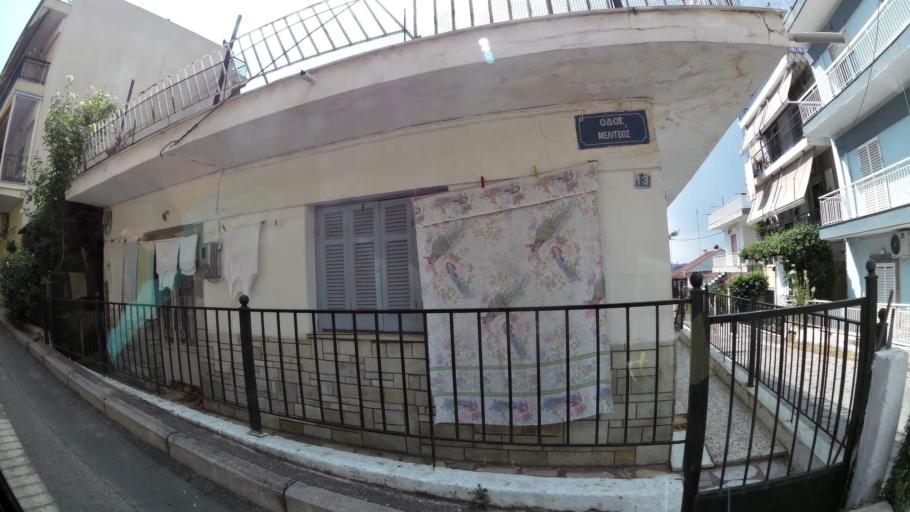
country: GR
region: Central Macedonia
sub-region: Nomos Thessalonikis
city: Stavroupoli
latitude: 40.6708
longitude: 22.9436
